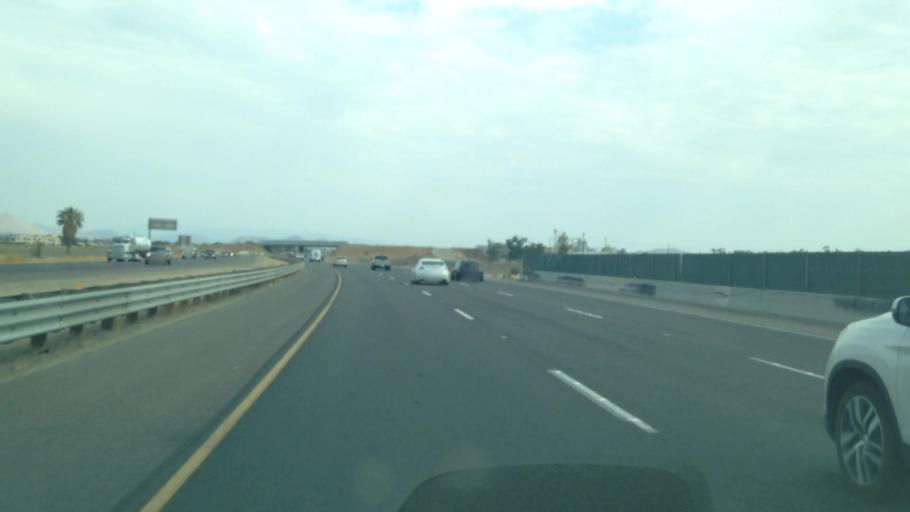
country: US
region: California
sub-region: Riverside County
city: Perris
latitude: 33.8291
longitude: -117.2451
